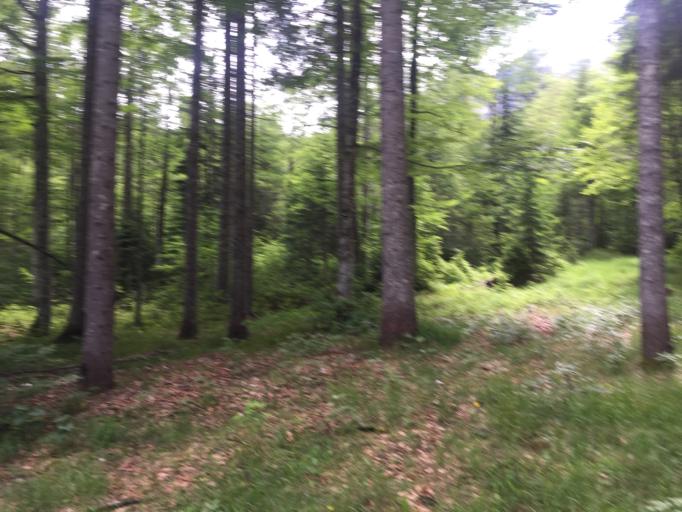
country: IT
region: Friuli Venezia Giulia
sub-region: Provincia di Udine
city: Malborghetto
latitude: 46.4526
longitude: 13.4930
